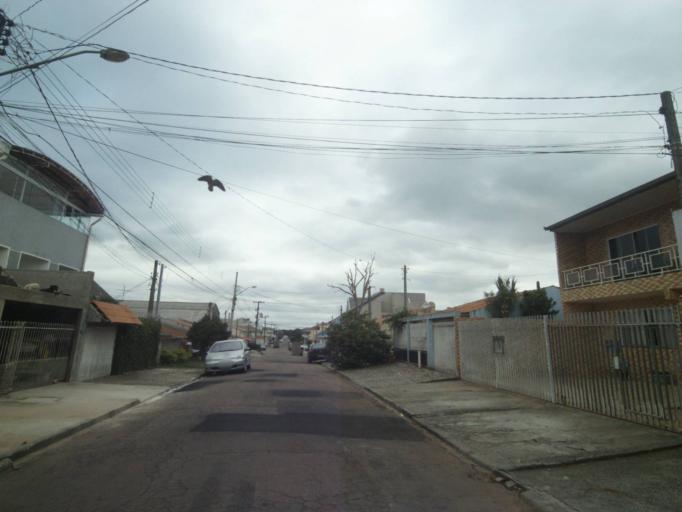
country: BR
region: Parana
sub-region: Sao Jose Dos Pinhais
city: Sao Jose dos Pinhais
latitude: -25.5449
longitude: -49.2604
